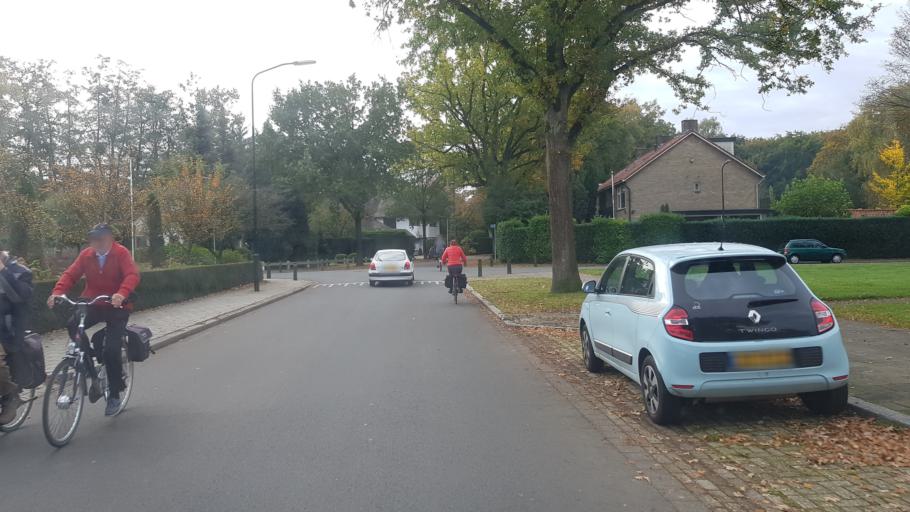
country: NL
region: Gelderland
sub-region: Gemeente Apeldoorn
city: Apeldoorn
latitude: 52.2272
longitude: 5.9679
